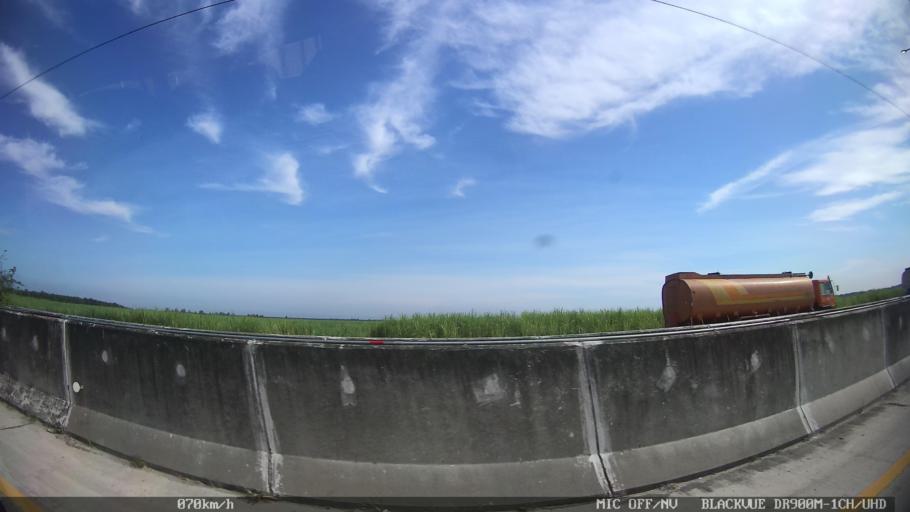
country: ID
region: North Sumatra
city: Sunggal
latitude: 3.6384
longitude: 98.6214
